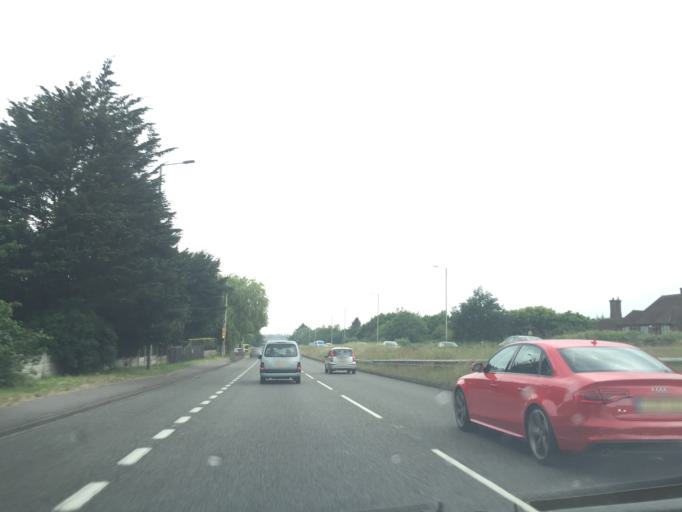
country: GB
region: England
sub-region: Poole
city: Canford Heath
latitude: 50.7387
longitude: -1.9680
